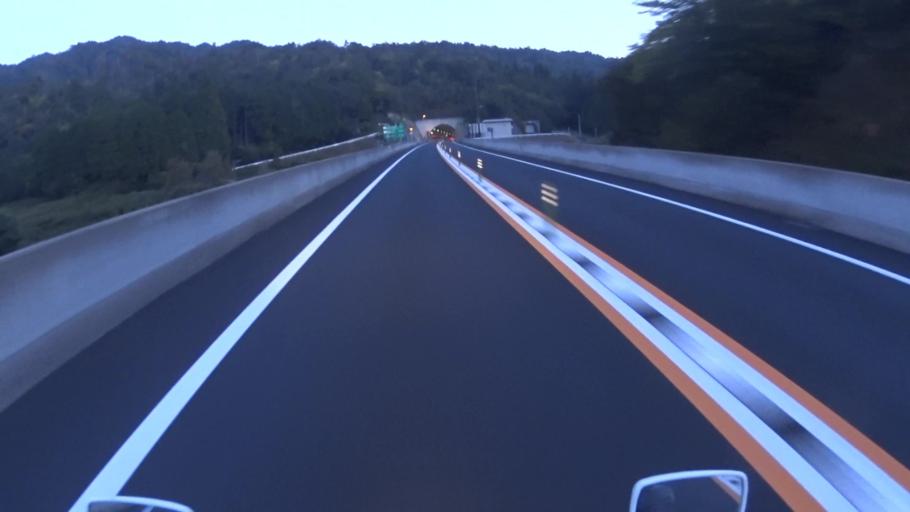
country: JP
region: Kyoto
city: Miyazu
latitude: 35.5431
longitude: 135.1551
